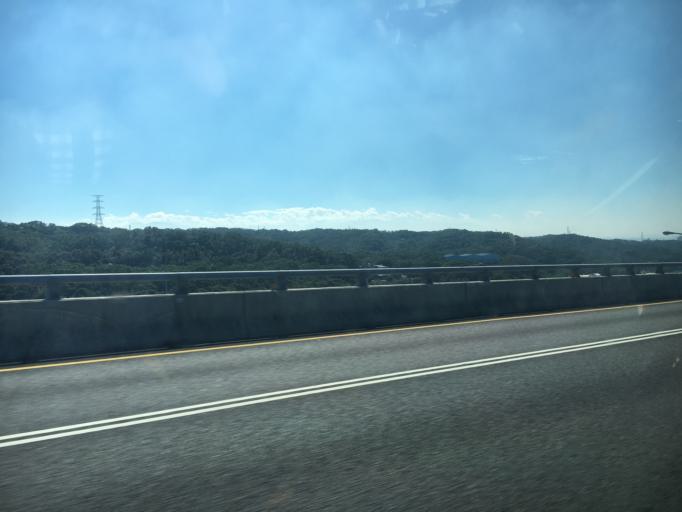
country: TW
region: Taiwan
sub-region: Taoyuan
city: Taoyuan
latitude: 25.0632
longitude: 121.3364
